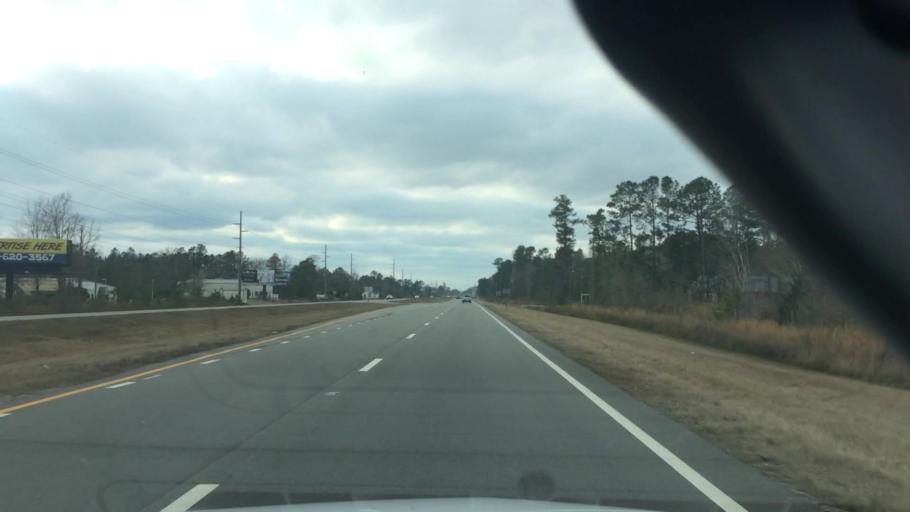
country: US
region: North Carolina
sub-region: Brunswick County
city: Carolina Shores
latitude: 33.9408
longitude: -78.5405
